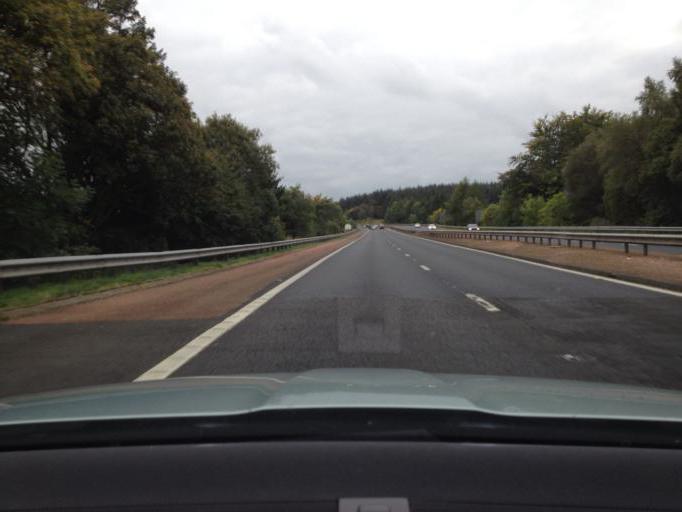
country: GB
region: Scotland
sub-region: Fife
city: Kelty
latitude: 56.1435
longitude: -3.3941
